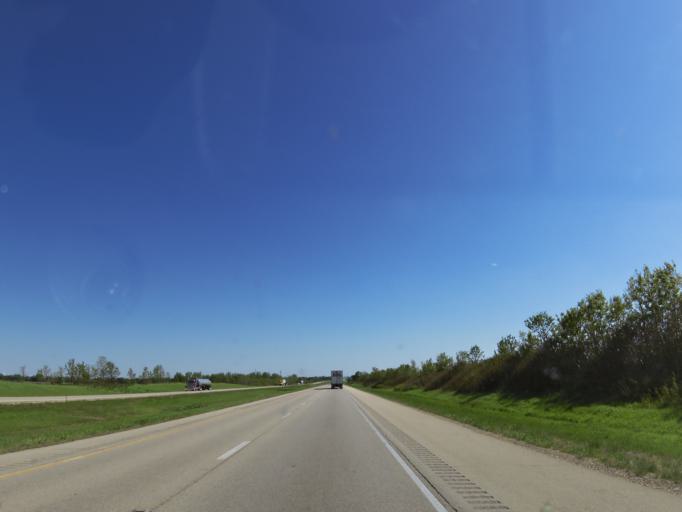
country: US
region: Illinois
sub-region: Ogle County
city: Rochelle
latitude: 41.8159
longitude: -89.0099
